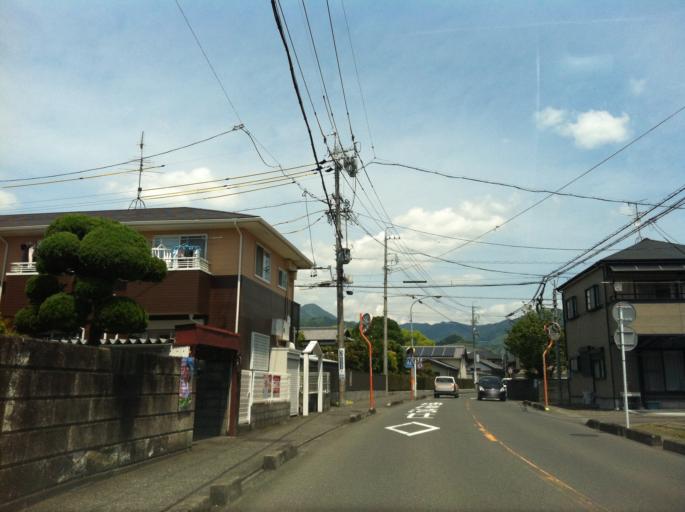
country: JP
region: Shizuoka
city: Shizuoka-shi
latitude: 35.0157
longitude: 138.4229
